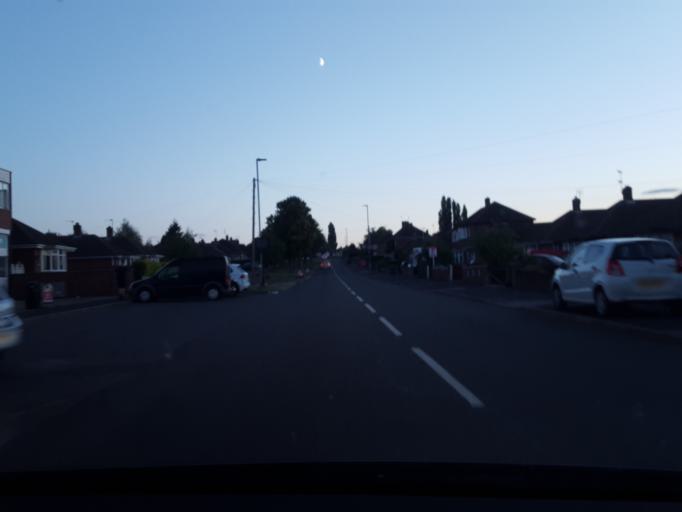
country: GB
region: England
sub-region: Leicestershire
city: Loughborough
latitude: 52.7547
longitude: -1.2124
